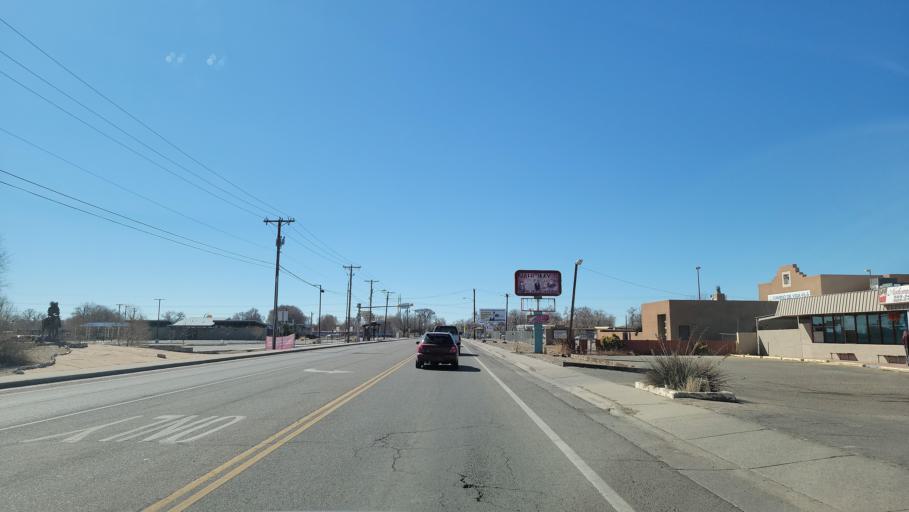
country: US
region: New Mexico
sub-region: Bernalillo County
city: South Valley
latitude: 35.0192
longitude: -106.6835
